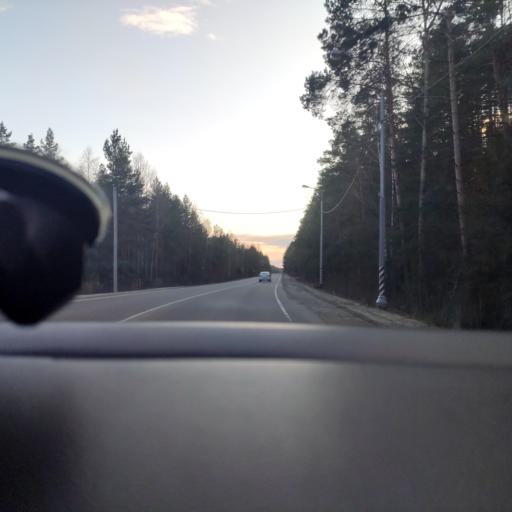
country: RU
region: Moskovskaya
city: Krasnyy Tkach
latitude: 55.4114
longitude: 39.1689
